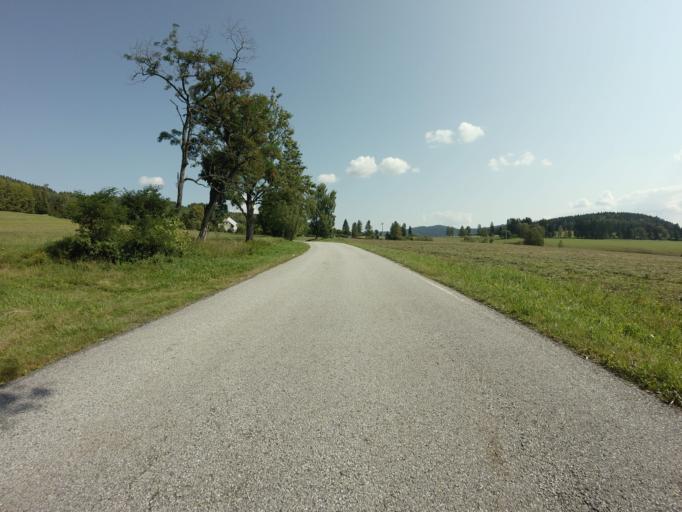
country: CZ
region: Jihocesky
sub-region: Okres Cesky Krumlov
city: Vyssi Brod
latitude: 48.6306
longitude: 14.3399
